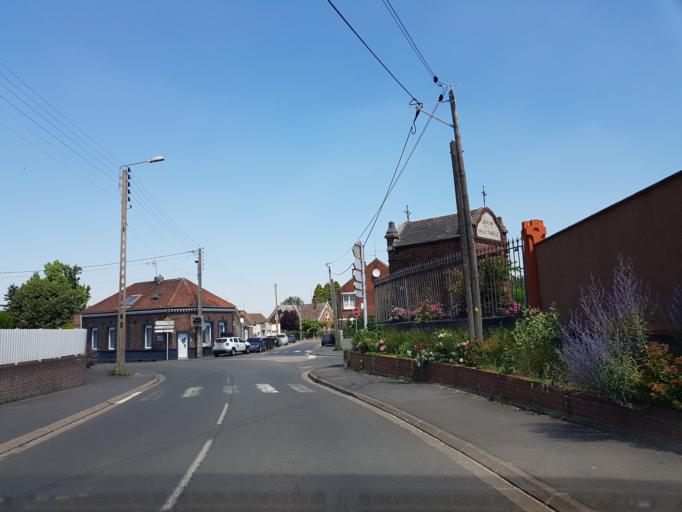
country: FR
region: Nord-Pas-de-Calais
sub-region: Departement du Nord
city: Neuville-sur-Escaut
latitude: 50.2978
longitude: 3.3570
